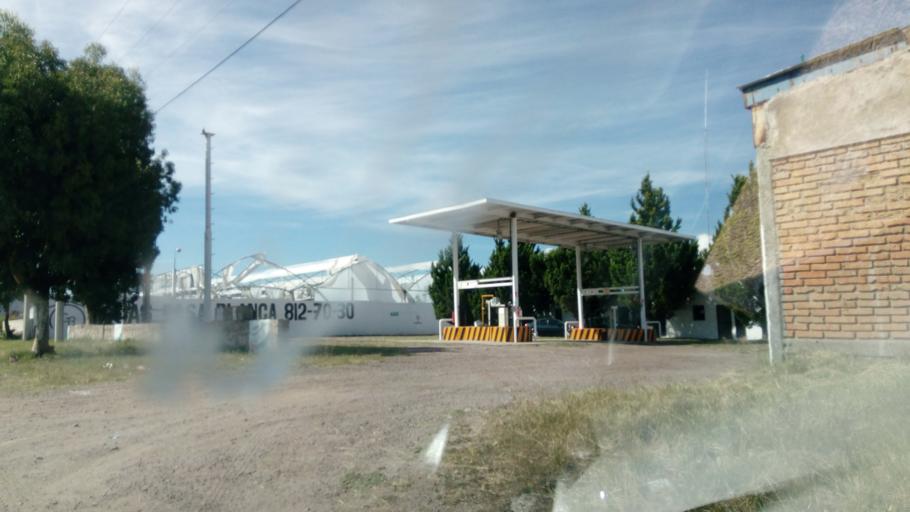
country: MX
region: Durango
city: Victoria de Durango
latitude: 24.1478
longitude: -104.7093
